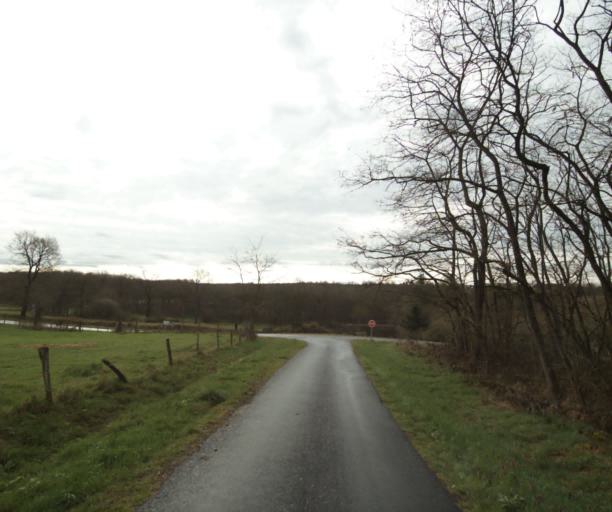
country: FR
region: Auvergne
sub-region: Departement de l'Allier
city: Toulon-sur-Allier
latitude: 46.5164
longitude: 3.3797
